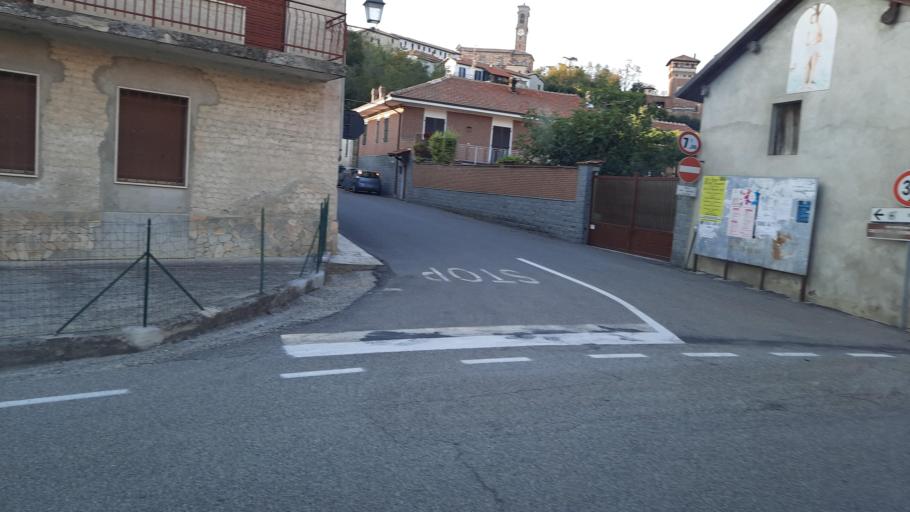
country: IT
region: Piedmont
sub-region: Provincia di Alessandria
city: Cereseto
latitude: 45.0843
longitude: 8.3166
